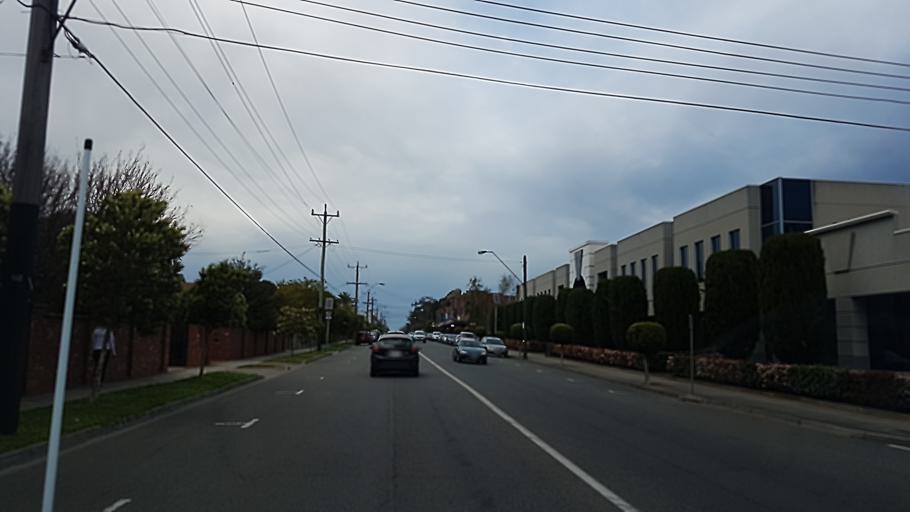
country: AU
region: Victoria
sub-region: Stonnington
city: Glen Iris
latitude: -37.8631
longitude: 145.0506
